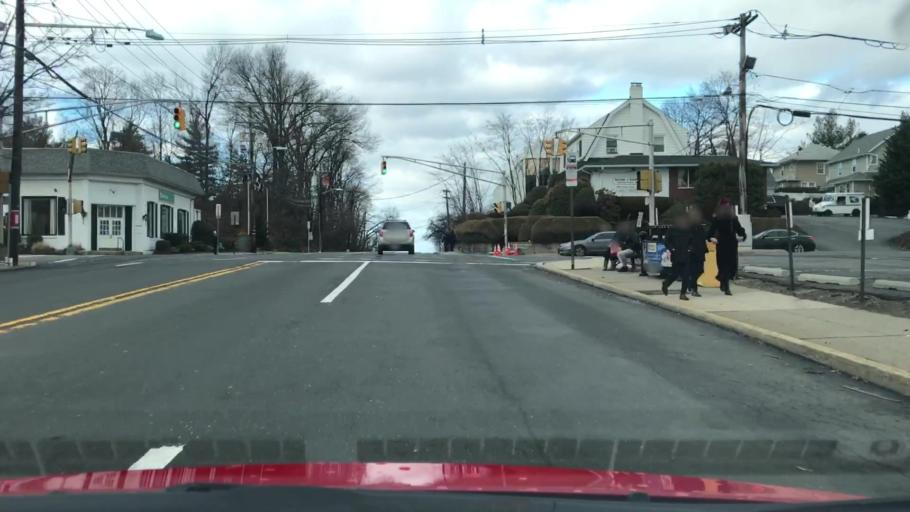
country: US
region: New Jersey
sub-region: Bergen County
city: Teaneck
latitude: 40.8866
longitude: -74.0145
